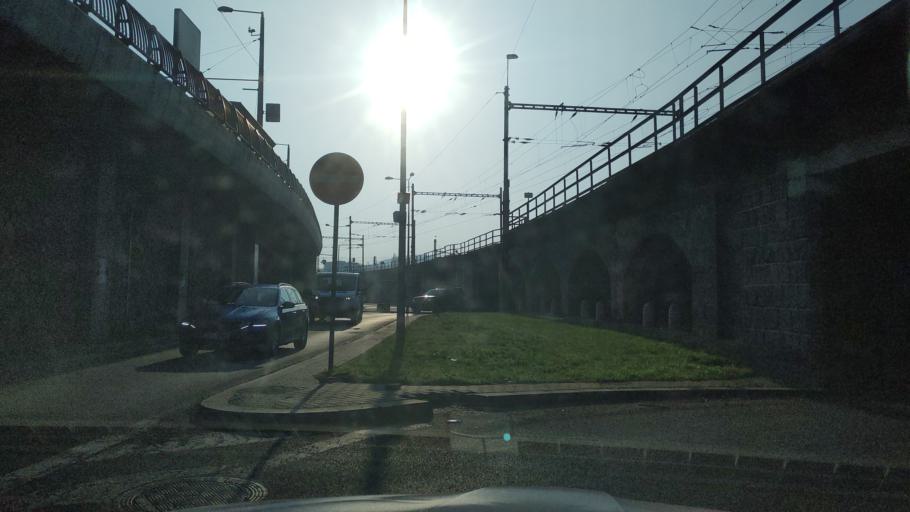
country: CZ
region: Ustecky
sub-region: Okres Usti nad Labem
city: Usti nad Labem
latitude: 50.6580
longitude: 14.0396
